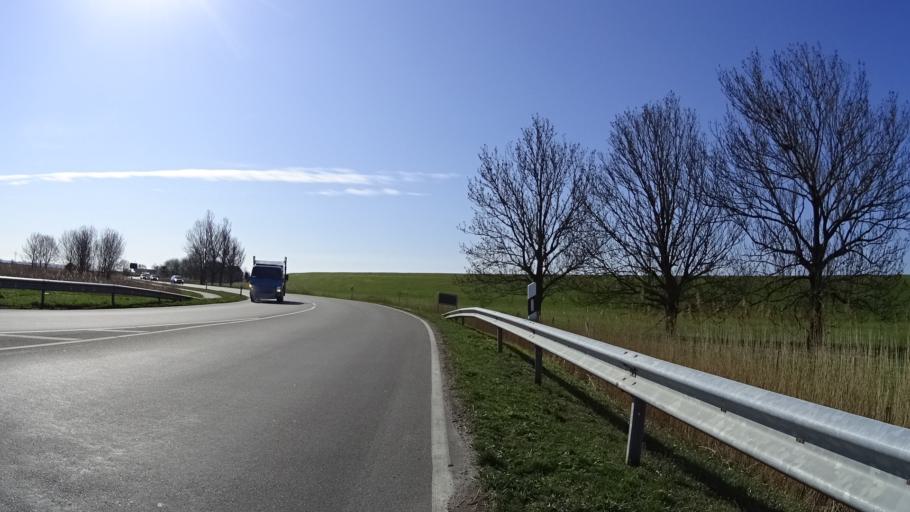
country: DE
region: Lower Saxony
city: Jemgum
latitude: 53.2954
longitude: 7.3967
